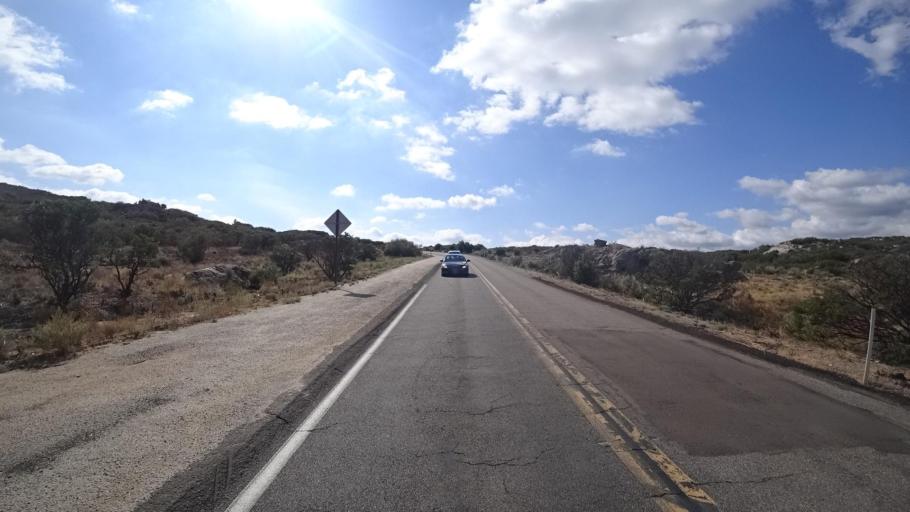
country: US
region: California
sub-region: San Diego County
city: Campo
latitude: 32.6903
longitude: -116.4907
